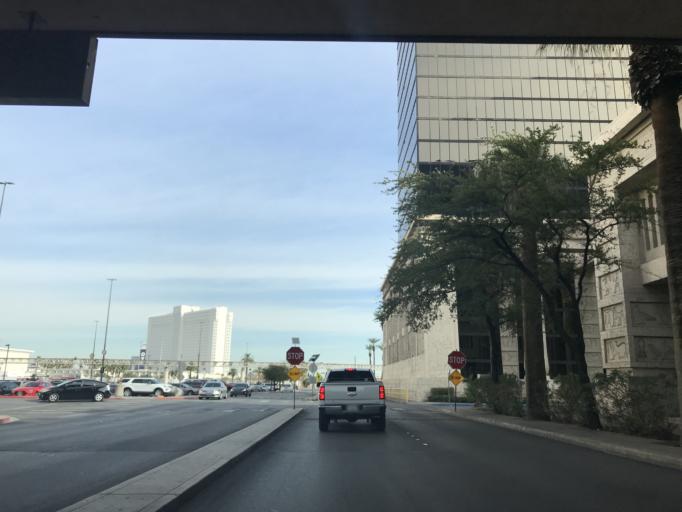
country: US
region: Nevada
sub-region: Clark County
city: Paradise
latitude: 36.0973
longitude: -115.1760
